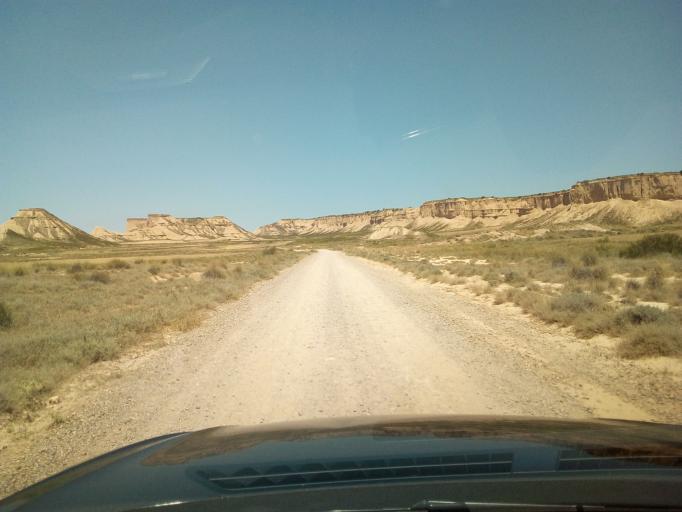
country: ES
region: Aragon
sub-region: Provincia de Zaragoza
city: Sadaba
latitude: 42.1919
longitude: -1.4124
